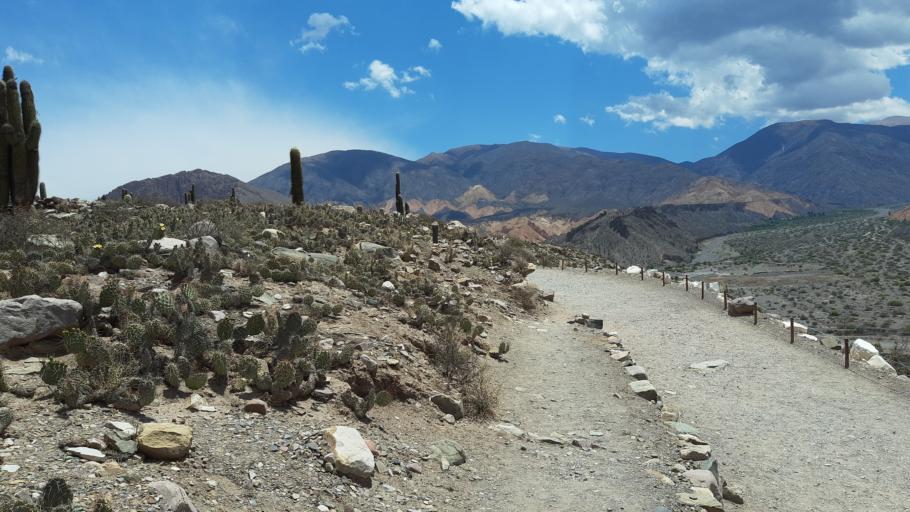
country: AR
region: Jujuy
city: Maimara
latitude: -23.5853
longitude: -65.4025
